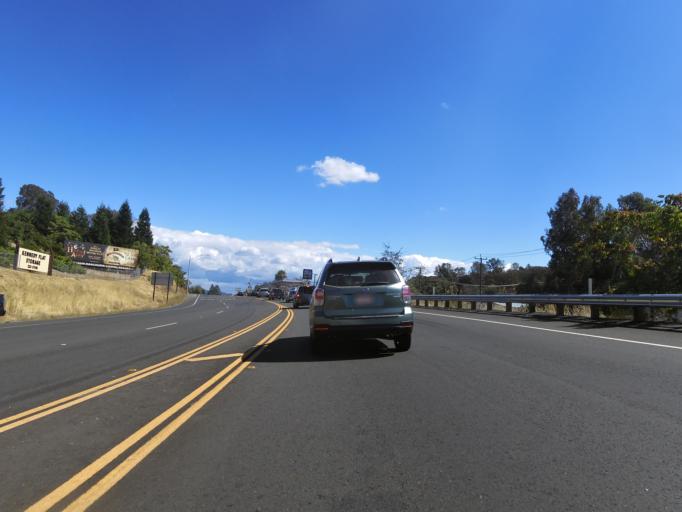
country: US
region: California
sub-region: Amador County
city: Jackson
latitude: 38.3651
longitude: -120.7926
